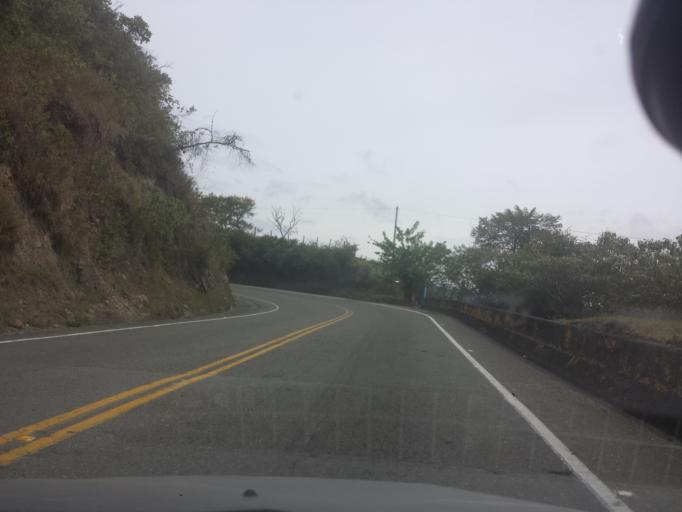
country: CO
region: Antioquia
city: Antioquia
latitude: 6.6129
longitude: -75.8525
